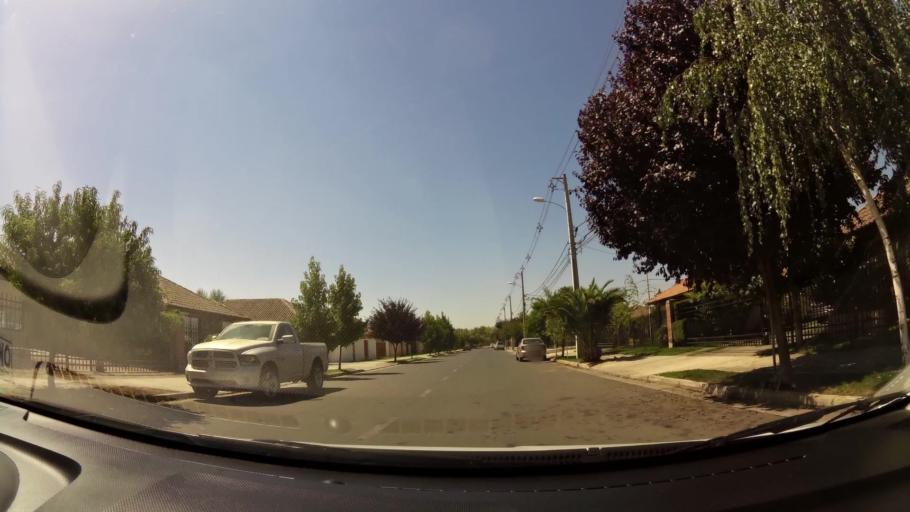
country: CL
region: Maule
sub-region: Provincia de Talca
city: Talca
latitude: -35.4321
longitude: -71.5990
